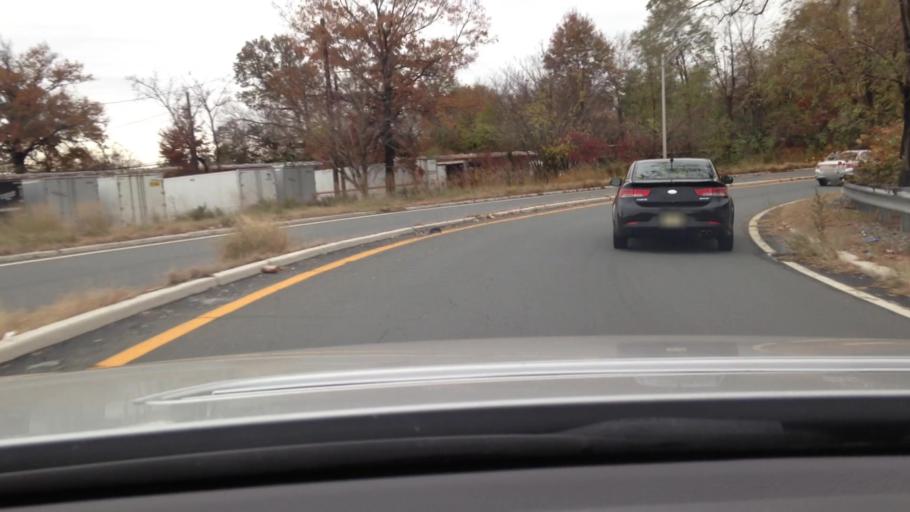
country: US
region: New Jersey
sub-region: Bergen County
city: Saddle Brook
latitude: 40.9023
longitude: -74.0954
